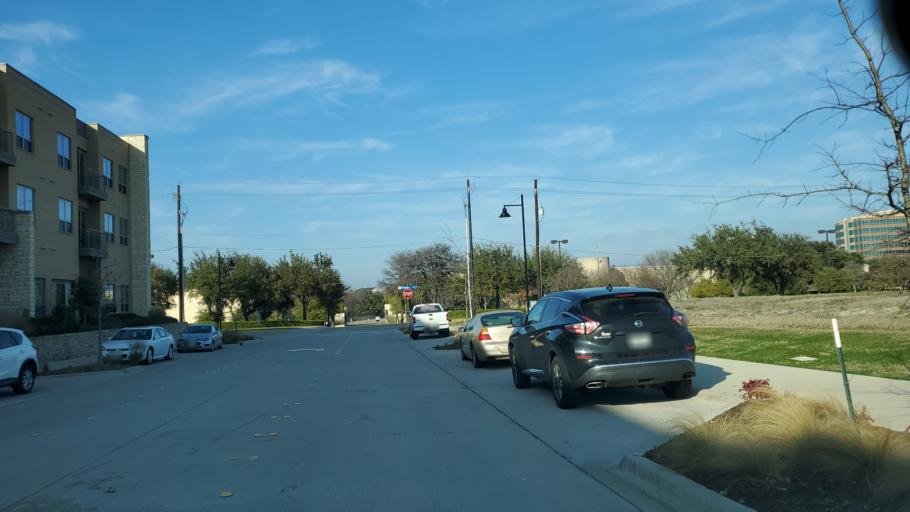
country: US
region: Texas
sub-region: Collin County
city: Plano
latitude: 32.9902
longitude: -96.7121
